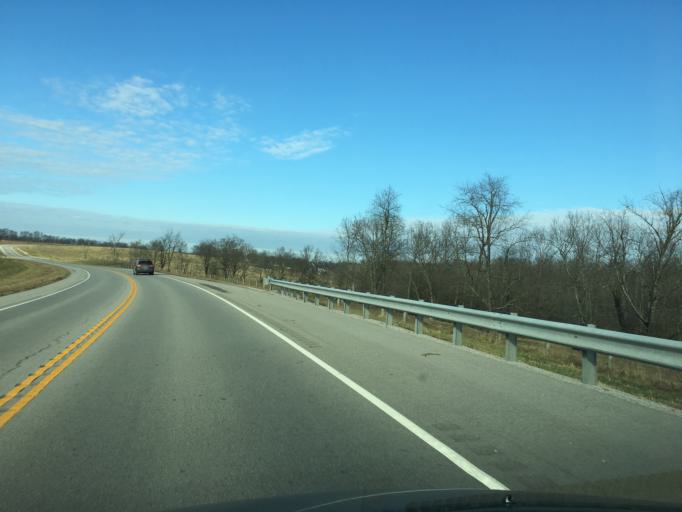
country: US
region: Kentucky
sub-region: Scott County
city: Georgetown
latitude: 38.2259
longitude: -84.5854
